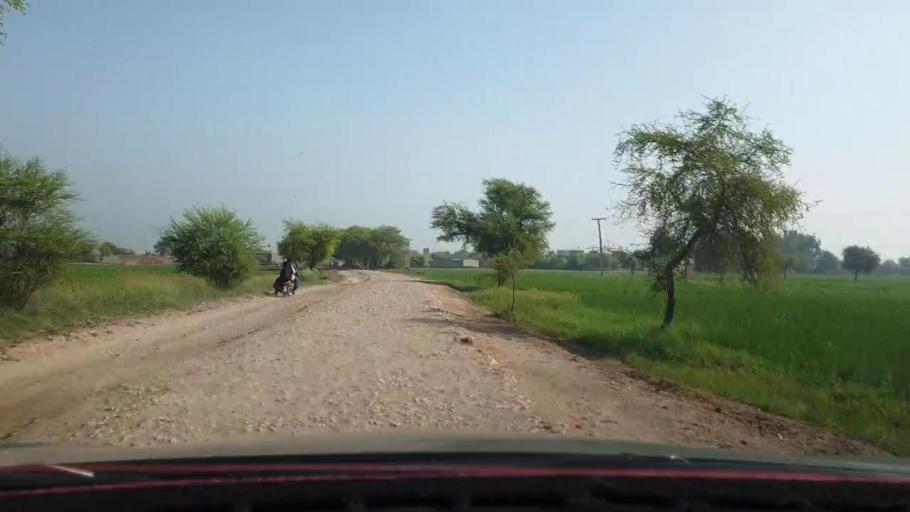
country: PK
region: Sindh
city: Nasirabad
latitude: 27.4591
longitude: 67.9182
